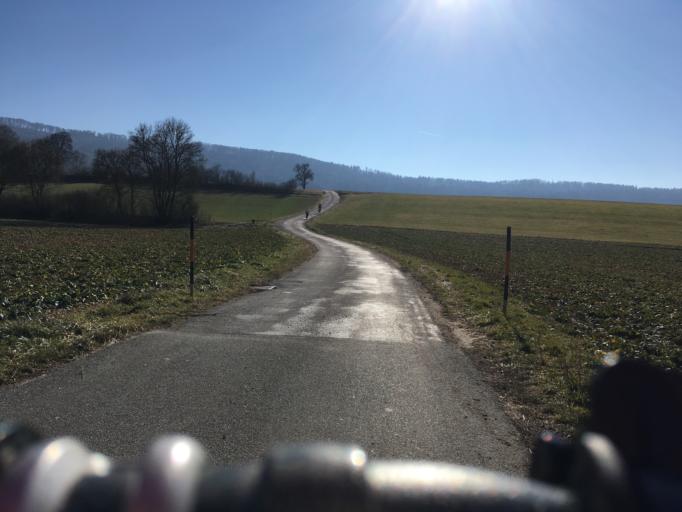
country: DE
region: Baden-Wuerttemberg
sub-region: Freiburg Region
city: Gottmadingen
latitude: 47.7199
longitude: 8.7703
